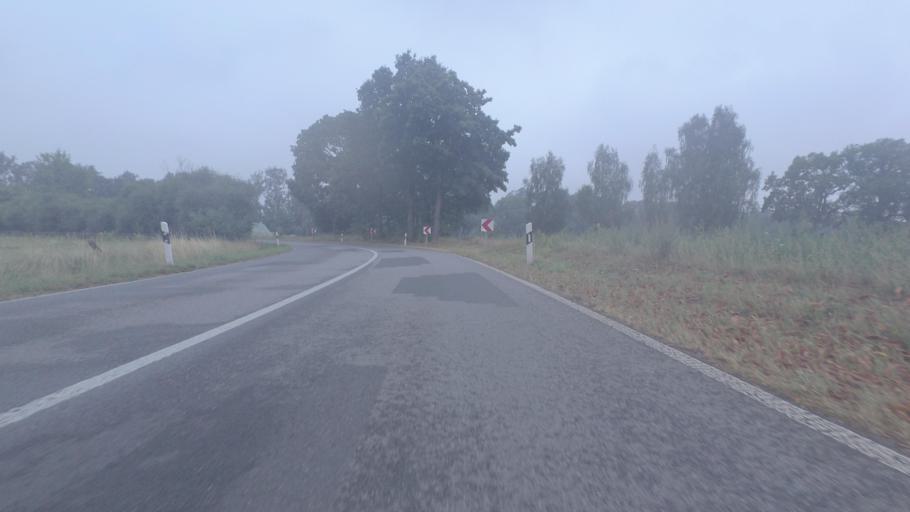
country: DE
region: Brandenburg
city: Heiligengrabe
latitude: 53.1468
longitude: 12.3408
